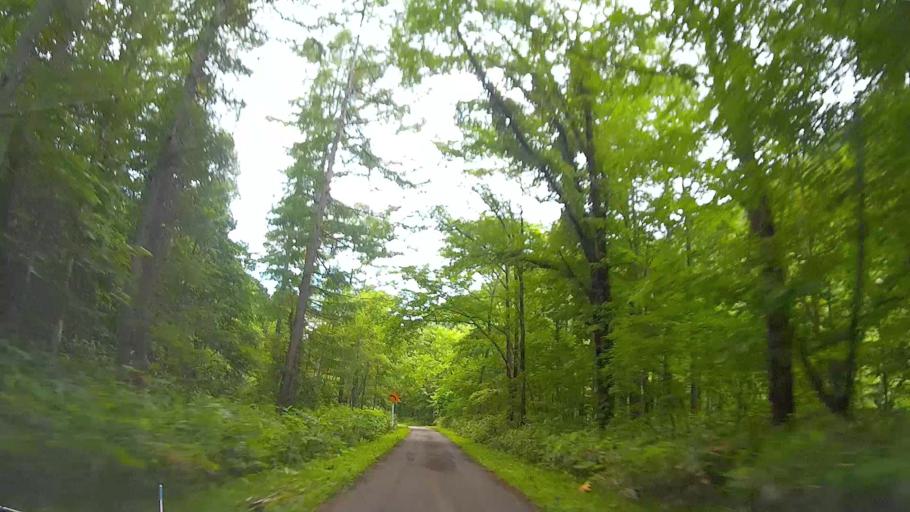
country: JP
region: Hokkaido
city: Nanae
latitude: 42.0445
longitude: 140.4872
